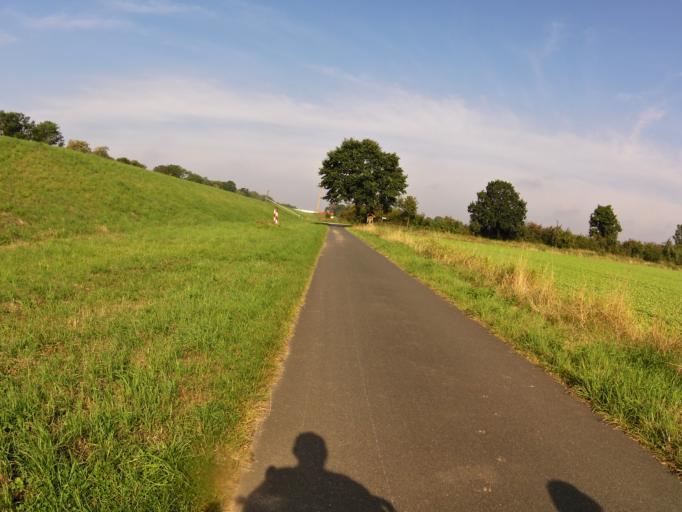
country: DE
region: Lower Saxony
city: Langwedel
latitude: 52.9666
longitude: 9.1640
